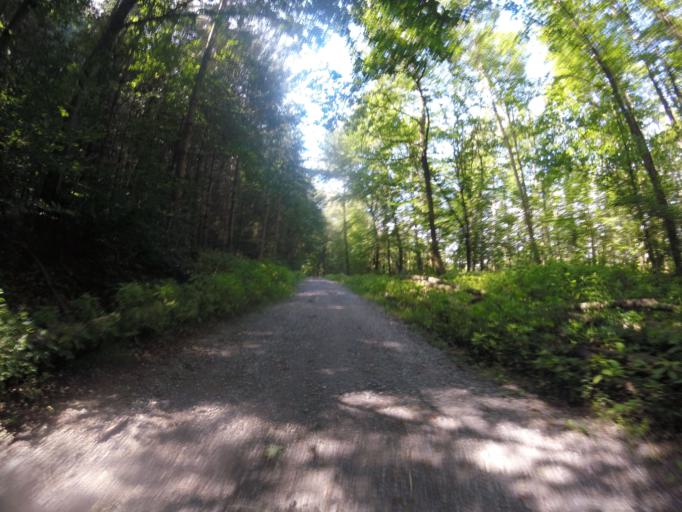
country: DE
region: Baden-Wuerttemberg
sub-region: Regierungsbezirk Stuttgart
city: Winnenden
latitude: 48.8439
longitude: 9.4149
